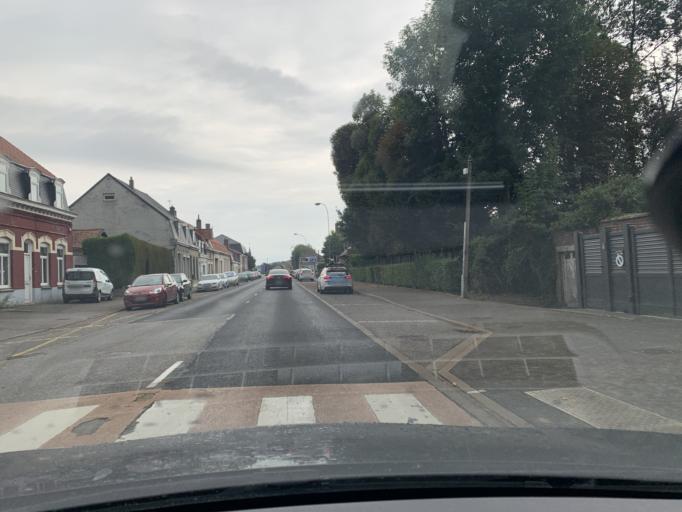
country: FR
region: Nord-Pas-de-Calais
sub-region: Departement du Nord
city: Bergues
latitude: 50.9603
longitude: 2.4335
